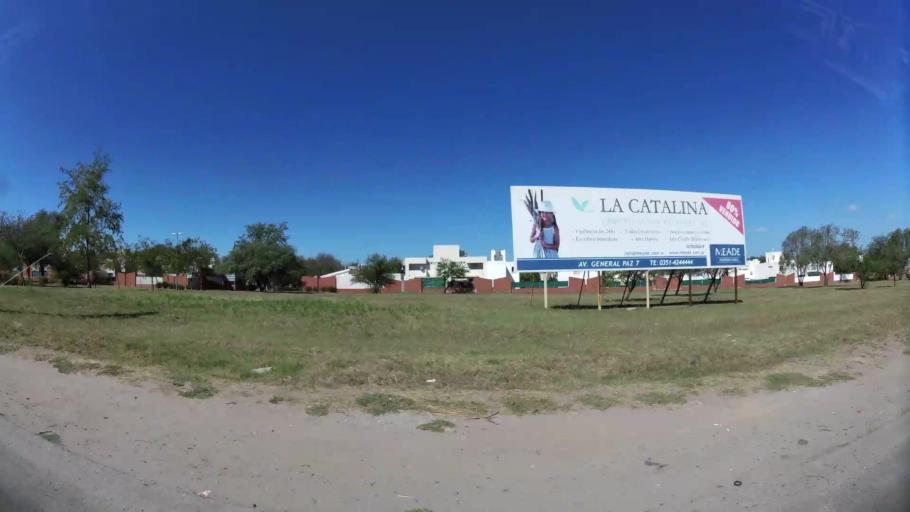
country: AR
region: Cordoba
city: Saldan
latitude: -31.3223
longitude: -64.2885
